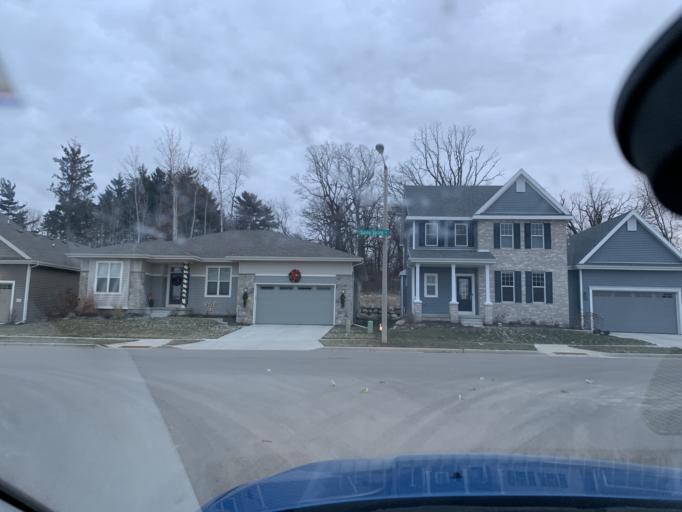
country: US
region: Wisconsin
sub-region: Dane County
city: Verona
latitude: 43.0496
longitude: -89.5554
